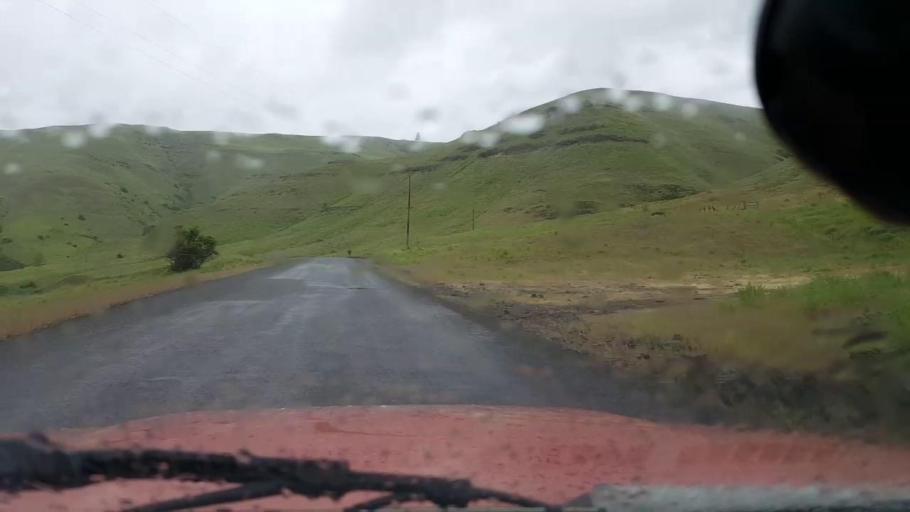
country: US
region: Washington
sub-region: Asotin County
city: Asotin
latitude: 46.0404
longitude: -117.2887
